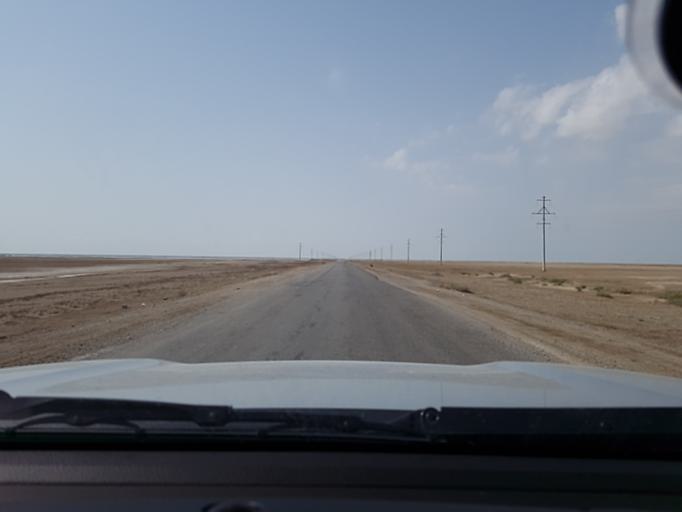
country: TM
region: Balkan
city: Gumdag
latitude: 39.0920
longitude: 54.5845
